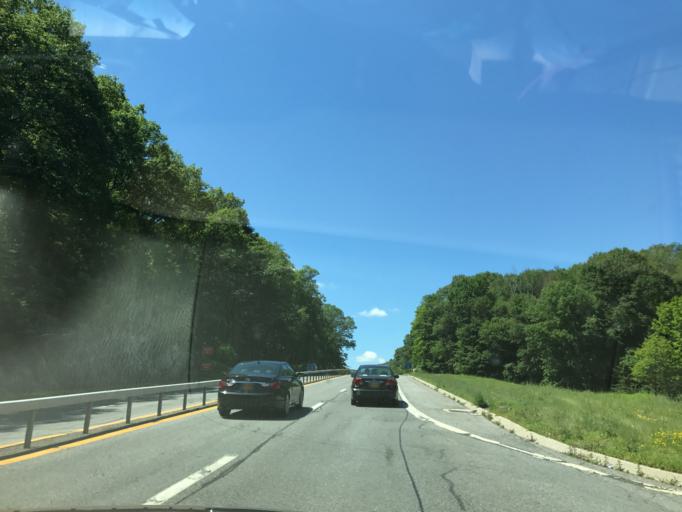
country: US
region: New York
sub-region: Dutchess County
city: Brinckerhoff
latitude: 41.4922
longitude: -73.8037
